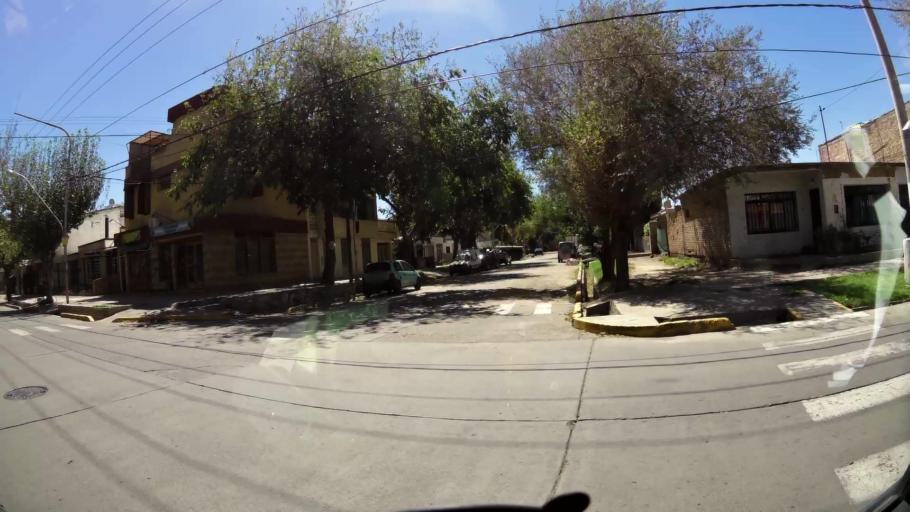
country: AR
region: Mendoza
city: Las Heras
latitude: -32.8604
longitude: -68.8471
